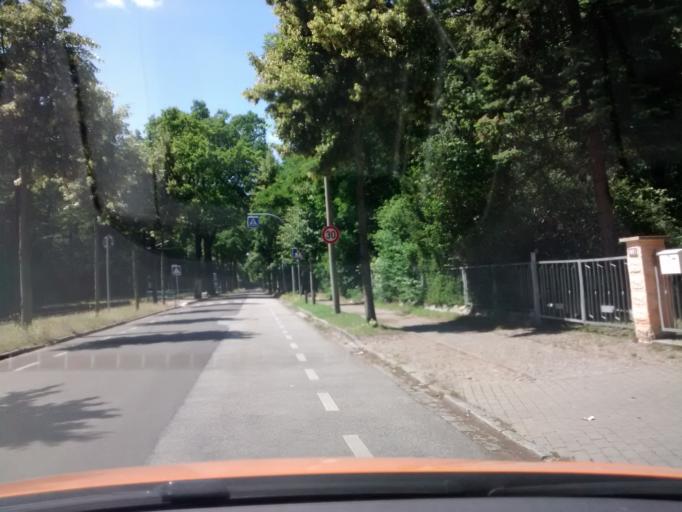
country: DE
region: Brandenburg
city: Potsdam
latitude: 52.3936
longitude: 13.1107
